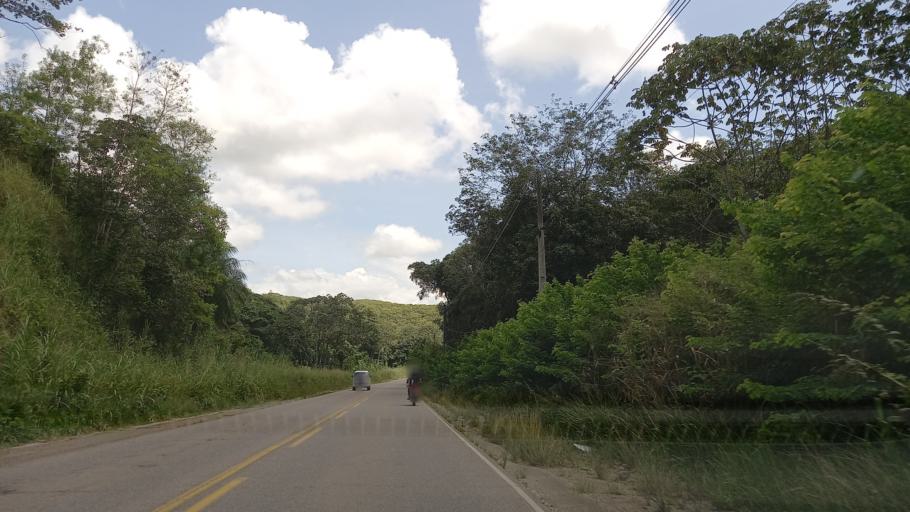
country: BR
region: Pernambuco
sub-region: Rio Formoso
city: Rio Formoso
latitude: -8.6470
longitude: -35.1248
